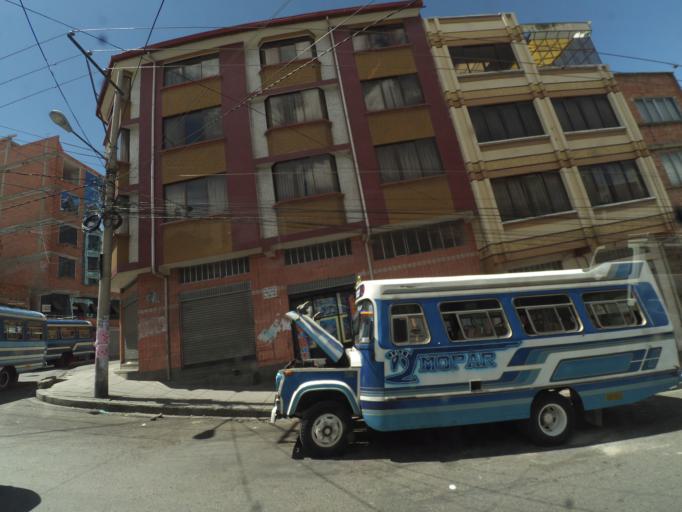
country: BO
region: La Paz
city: La Paz
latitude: -16.4960
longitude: -68.1552
